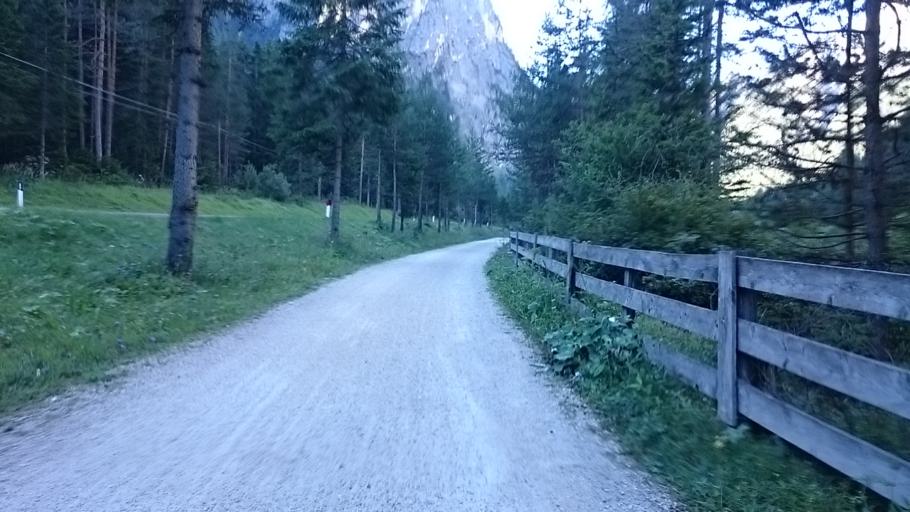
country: IT
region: Trentino-Alto Adige
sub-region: Bolzano
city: Dobbiaco
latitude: 46.6857
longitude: 12.2243
